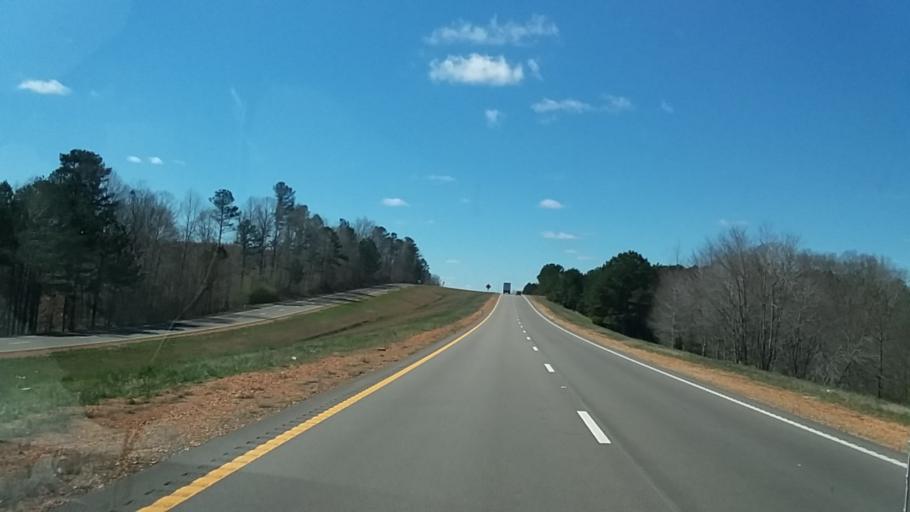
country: US
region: Mississippi
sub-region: Alcorn County
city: Farmington
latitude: 34.8553
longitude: -88.3689
